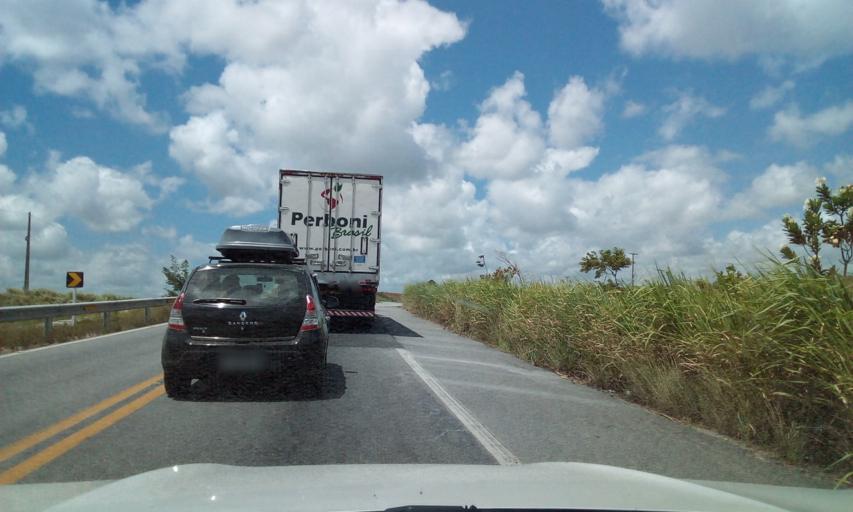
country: BR
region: Alagoas
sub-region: Sao Miguel Dos Campos
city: Sao Miguel dos Campos
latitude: -9.6845
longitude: -36.0373
